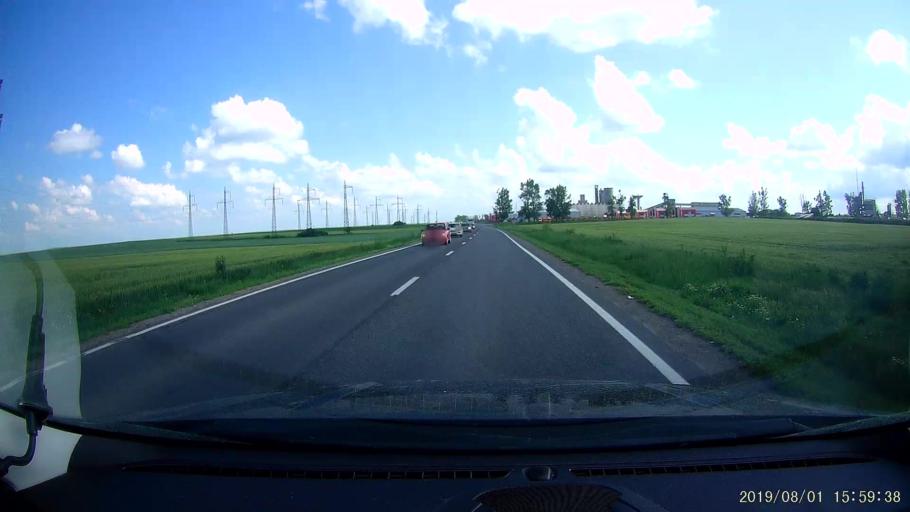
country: RO
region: Ialomita
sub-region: Comuna Slobozia
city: Slobozia
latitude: 44.5443
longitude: 27.3846
